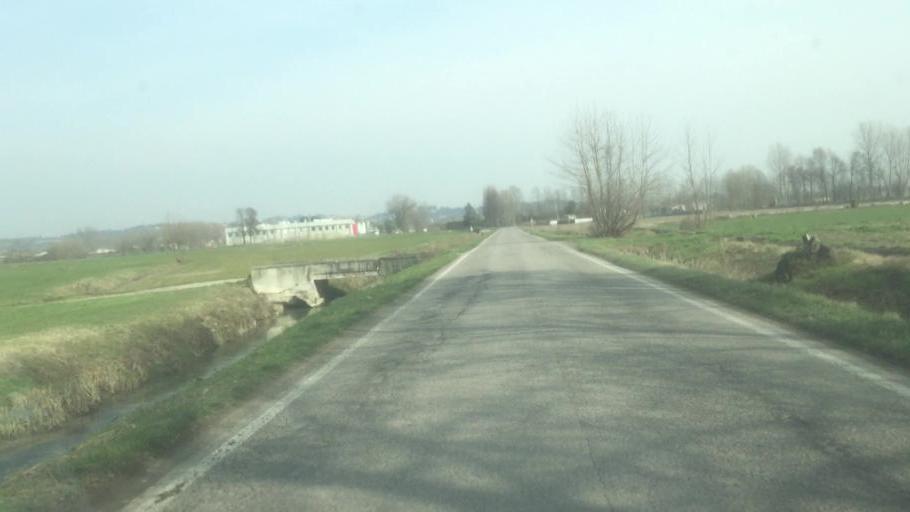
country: IT
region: Lombardy
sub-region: Provincia di Mantova
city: Cerlongo
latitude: 45.2943
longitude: 10.6340
